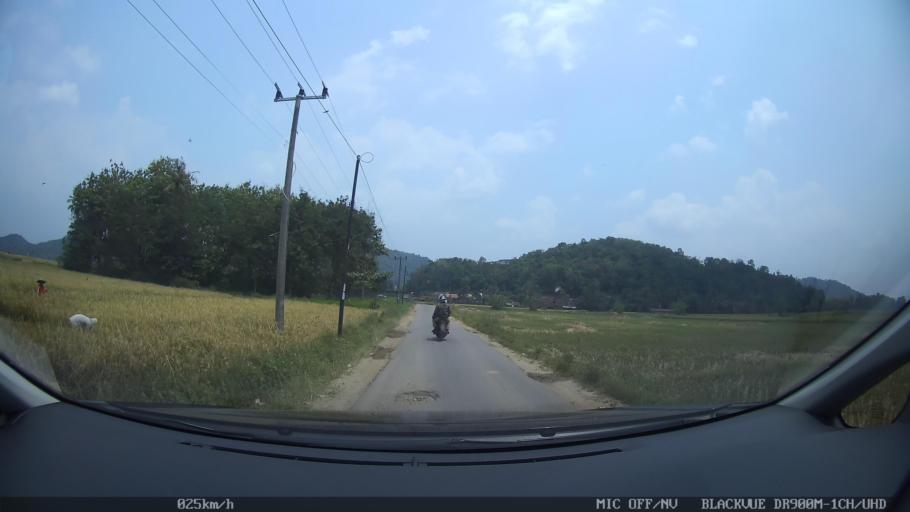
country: ID
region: Lampung
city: Pringsewu
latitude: -5.3728
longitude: 104.9976
